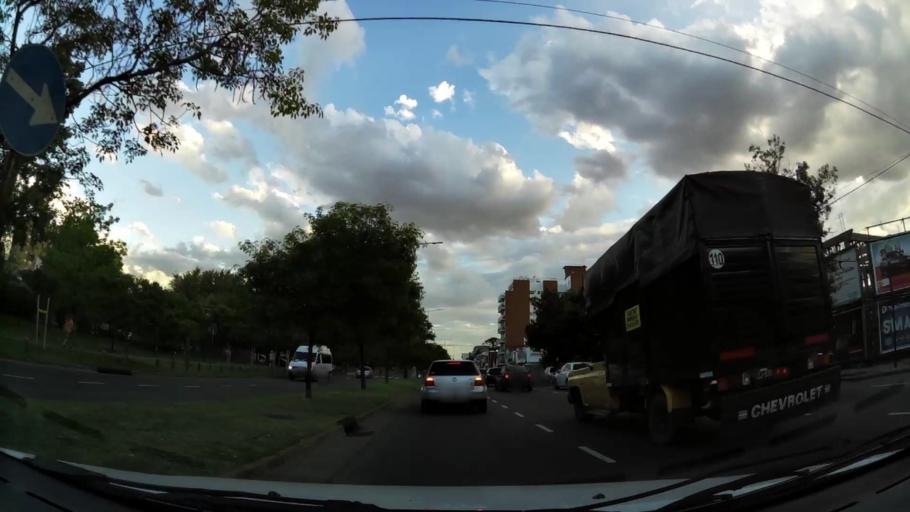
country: AR
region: Buenos Aires
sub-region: Partido de General San Martin
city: General San Martin
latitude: -34.5580
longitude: -58.4866
